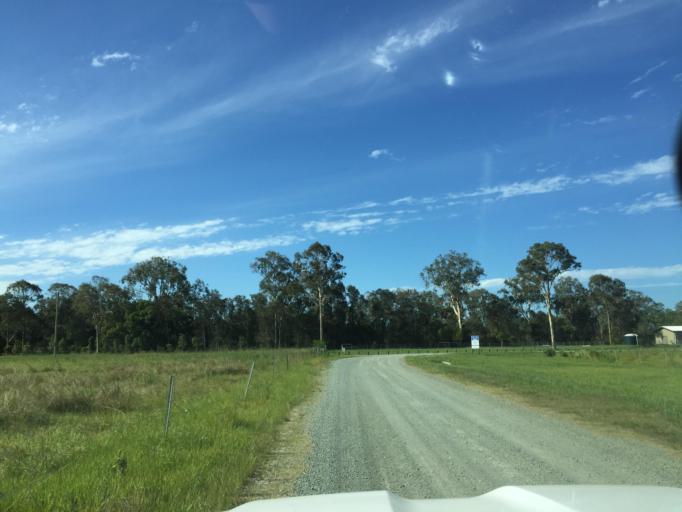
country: AU
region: Queensland
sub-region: Moreton Bay
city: Morayfield
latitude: -27.1076
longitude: 152.9930
